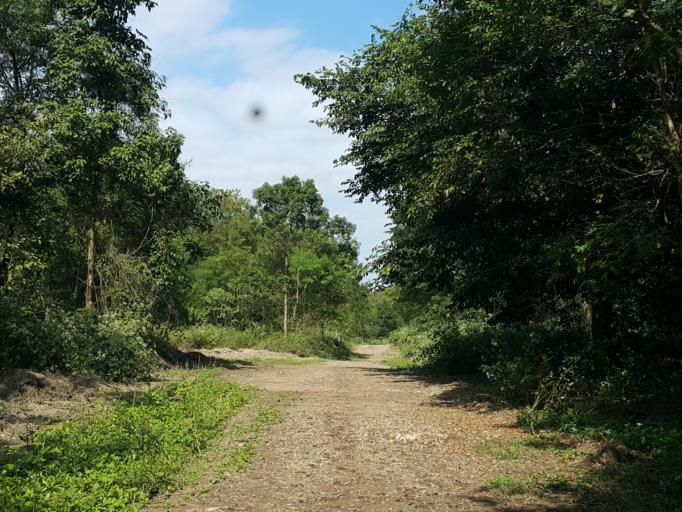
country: TH
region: Lampang
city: Mae Mo
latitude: 18.3385
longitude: 99.7688
